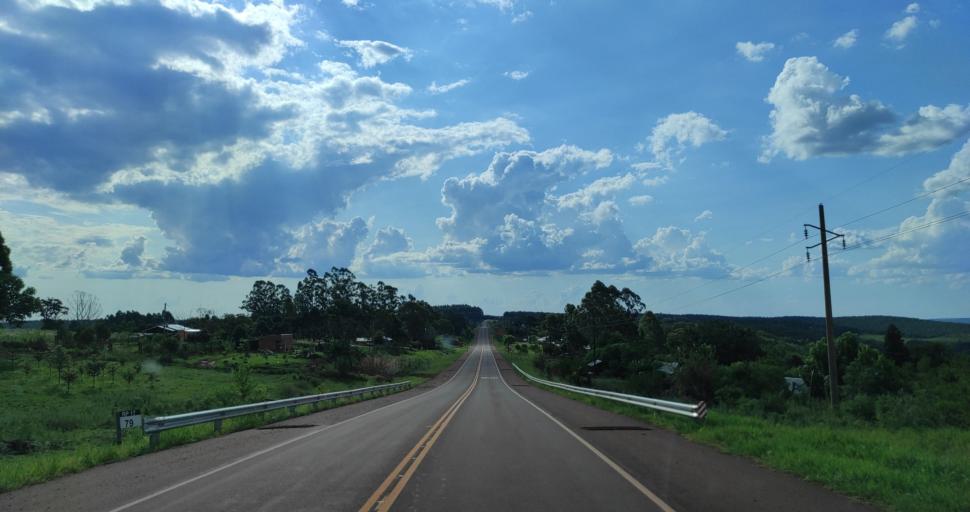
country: AR
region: Misiones
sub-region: Departamento de San Pedro
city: San Pedro
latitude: -26.3742
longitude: -53.9299
